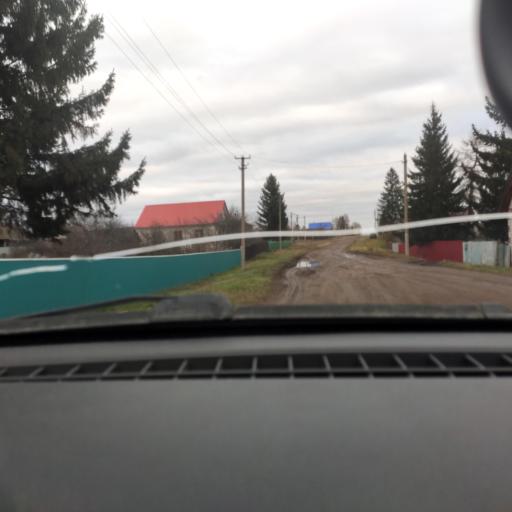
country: RU
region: Bashkortostan
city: Ulukulevo
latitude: 54.4390
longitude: 56.4576
